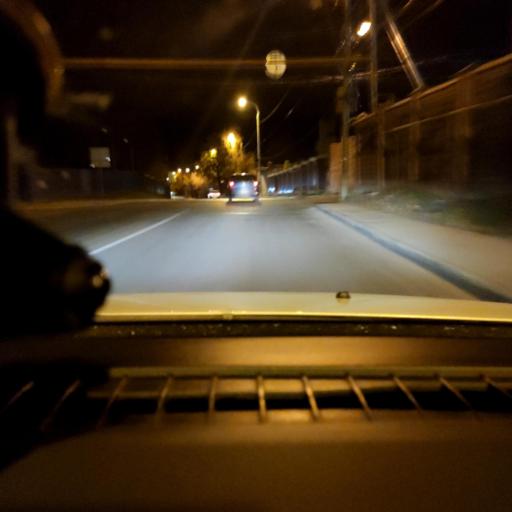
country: RU
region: Samara
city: Samara
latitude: 53.2705
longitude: 50.1958
